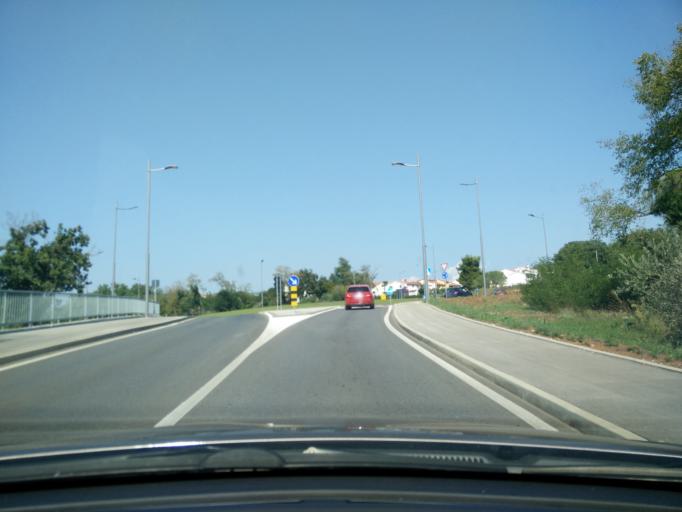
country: HR
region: Istarska
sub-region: Grad Porec
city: Porec
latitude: 45.2438
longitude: 13.6075
